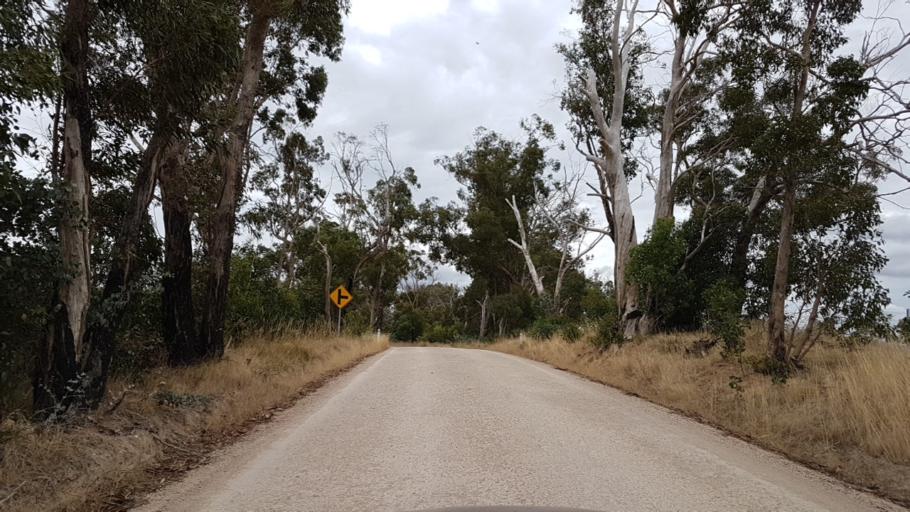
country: AU
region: South Australia
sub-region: Adelaide Hills
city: Gumeracha
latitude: -34.7997
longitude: 138.8152
